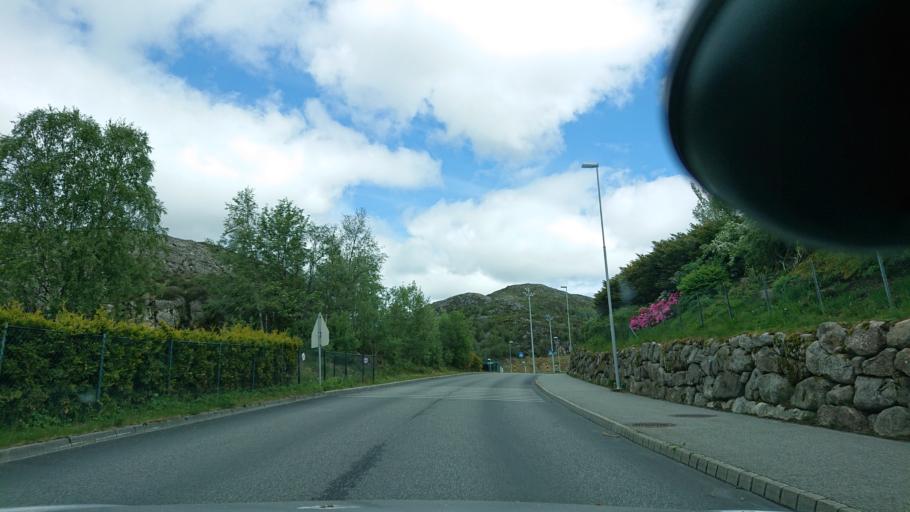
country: NO
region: Rogaland
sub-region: Gjesdal
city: Algard
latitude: 58.7731
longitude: 5.8657
